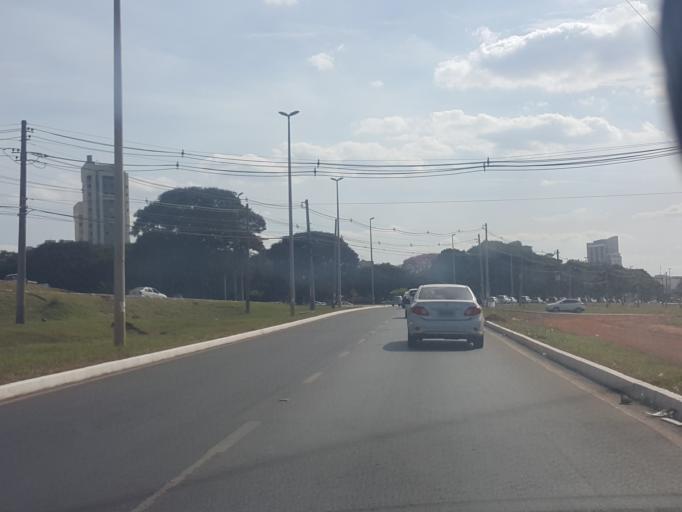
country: BR
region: Federal District
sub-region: Brasilia
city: Brasilia
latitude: -15.8306
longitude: -48.0490
